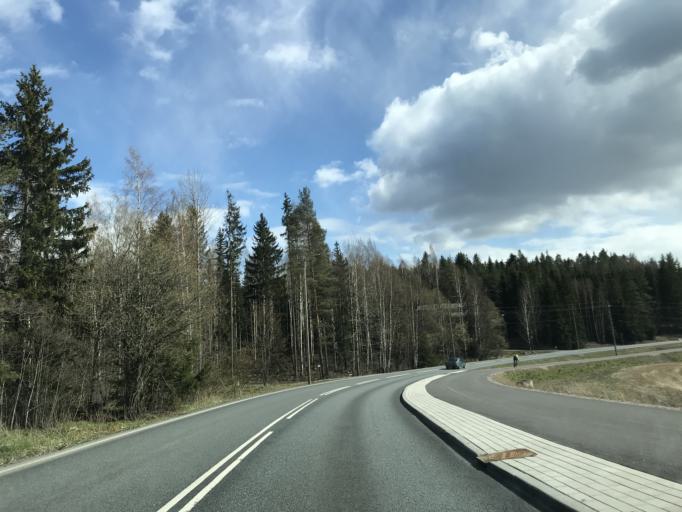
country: FI
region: Uusimaa
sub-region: Helsinki
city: Jaervenpaeae
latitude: 60.4851
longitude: 25.0426
